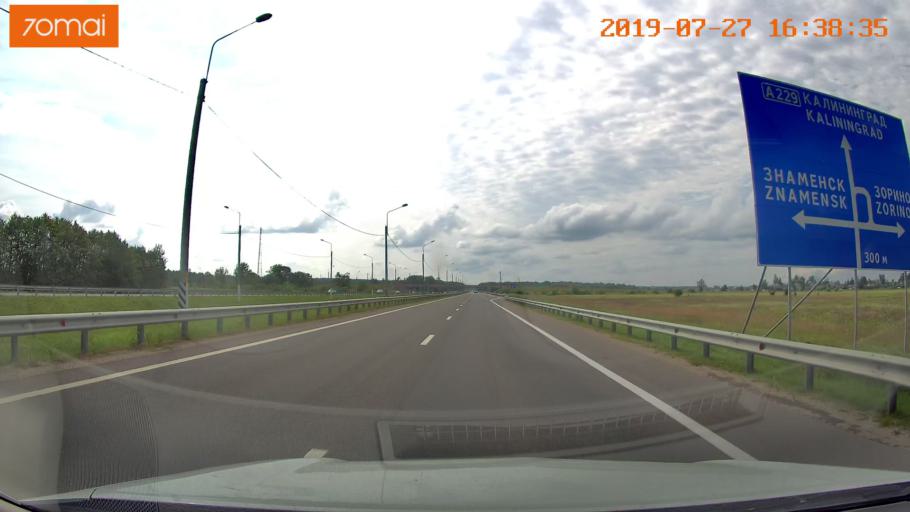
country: RU
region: Kaliningrad
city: Gvardeysk
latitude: 54.6490
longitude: 21.2240
